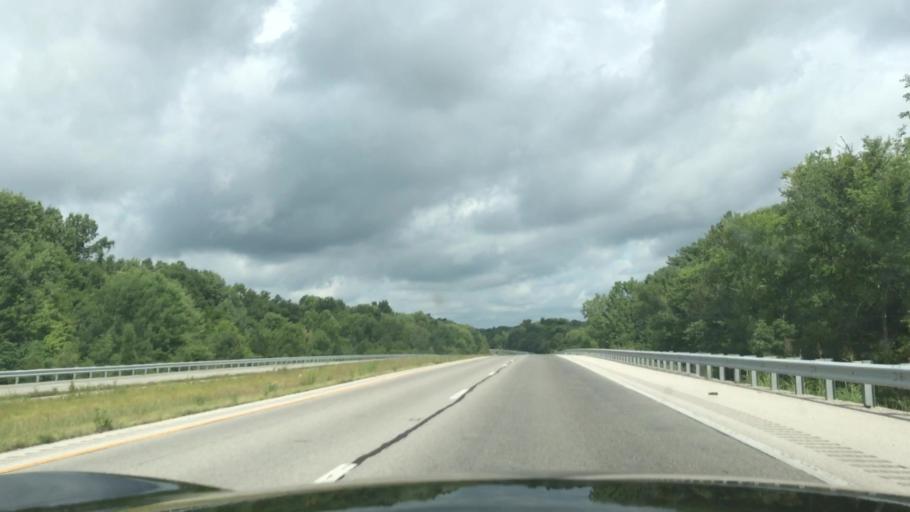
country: US
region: Kentucky
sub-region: Warren County
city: Bowling Green
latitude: 37.0279
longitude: -86.5356
